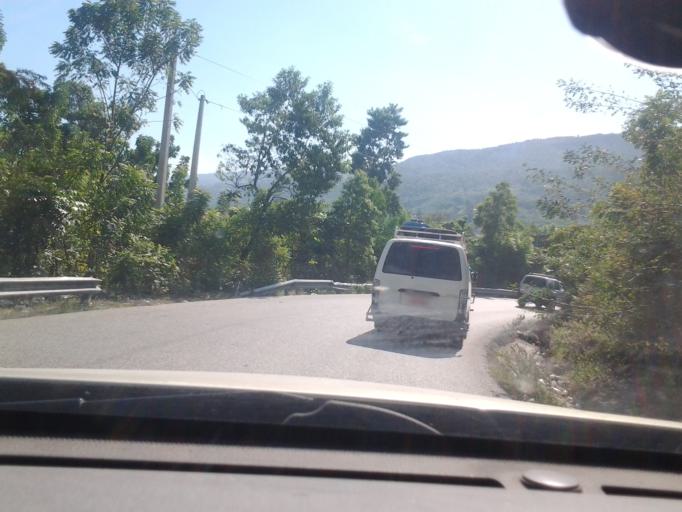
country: HT
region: Sud-Est
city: Jacmel
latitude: 18.2762
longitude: -72.5653
